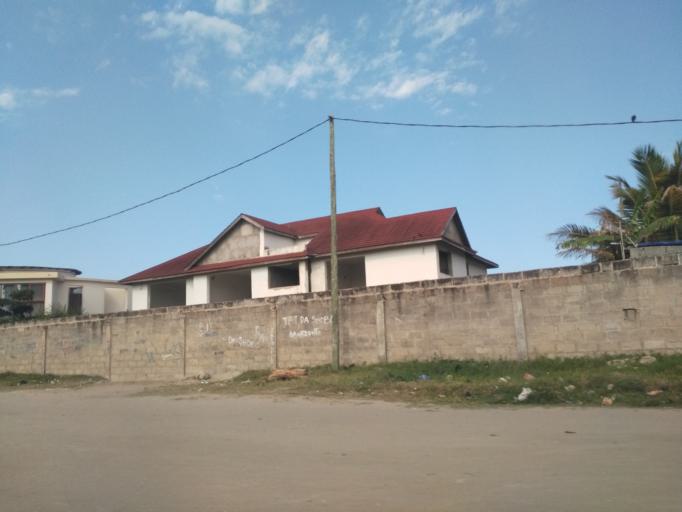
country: TZ
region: Dar es Salaam
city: Magomeni
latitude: -6.7650
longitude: 39.2648
